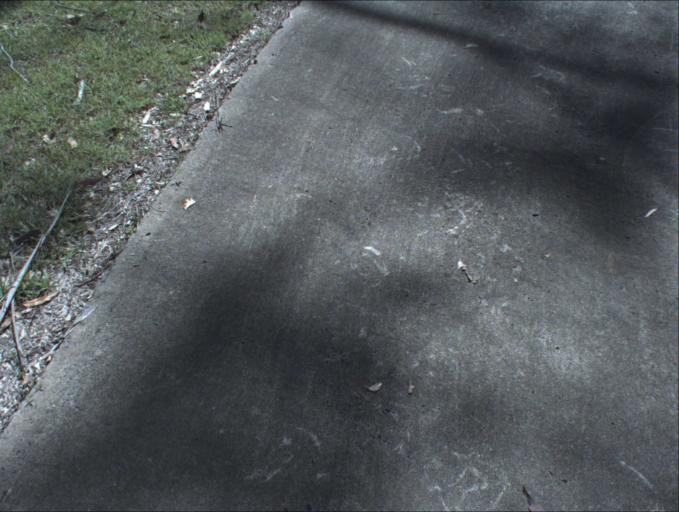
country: AU
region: Queensland
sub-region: Logan
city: Cedar Vale
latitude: -27.8598
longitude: 152.9788
